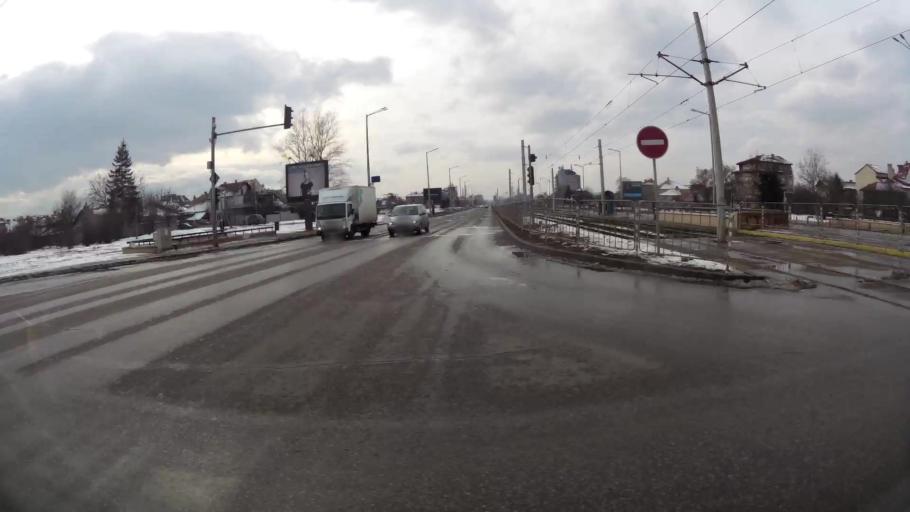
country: BG
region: Sofia-Capital
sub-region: Stolichna Obshtina
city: Sofia
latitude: 42.7030
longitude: 23.3868
